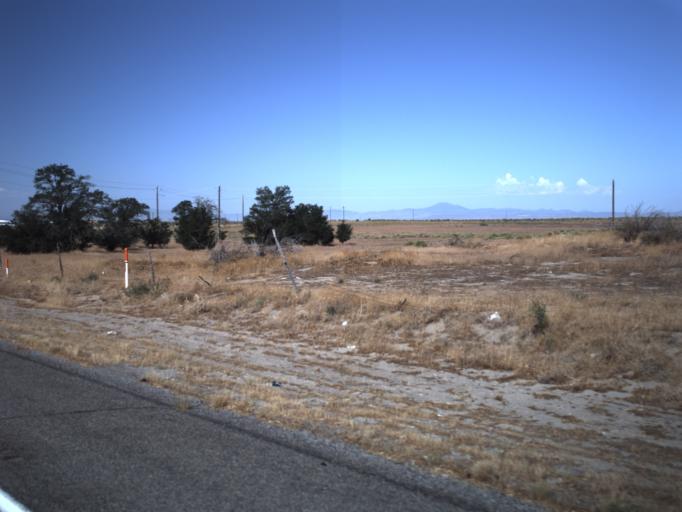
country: US
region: Utah
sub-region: Millard County
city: Delta
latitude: 39.3750
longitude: -112.5339
